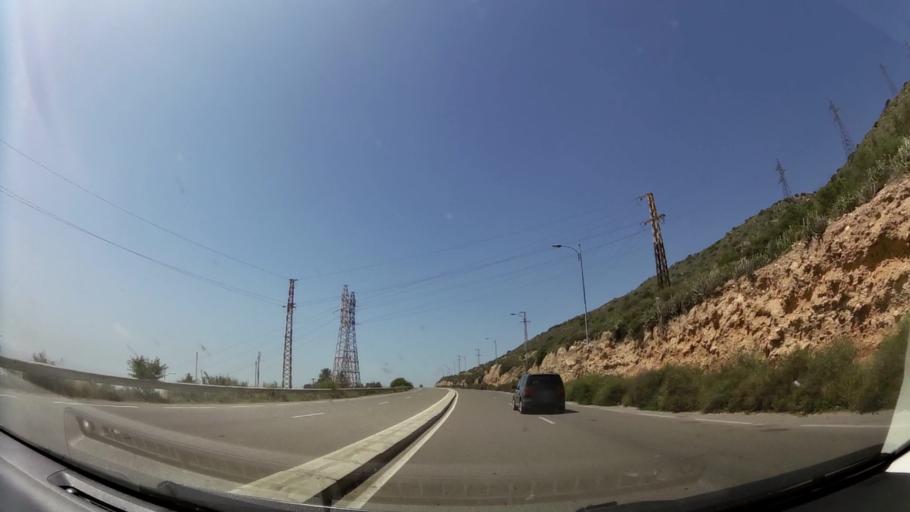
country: MA
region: Souss-Massa-Draa
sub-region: Agadir-Ida-ou-Tnan
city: Agadir
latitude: 30.4336
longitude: -9.6369
